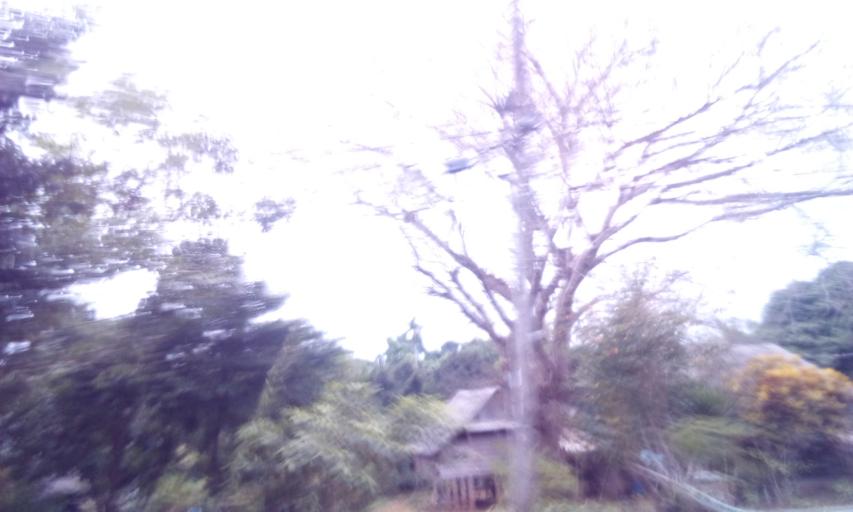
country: TH
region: Trat
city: Laem Ngop
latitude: 12.2511
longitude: 102.2920
